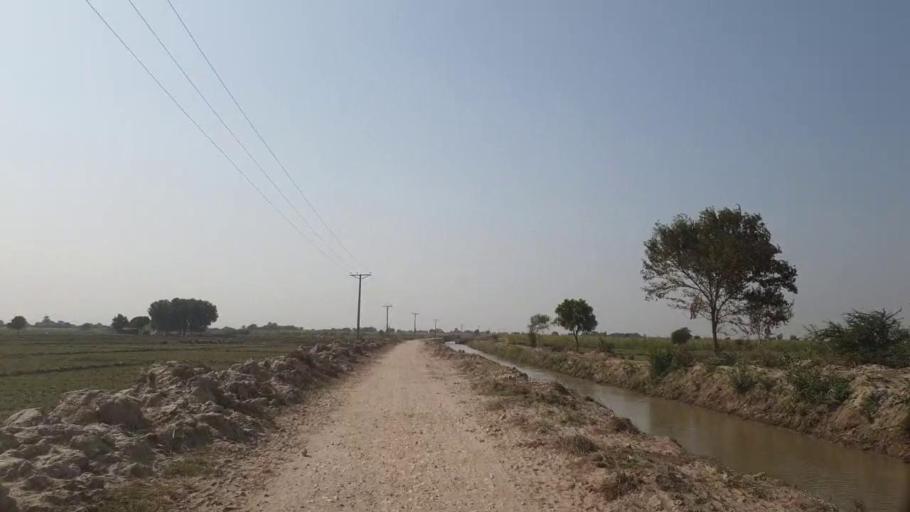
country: PK
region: Sindh
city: Bulri
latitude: 24.9524
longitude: 68.3795
